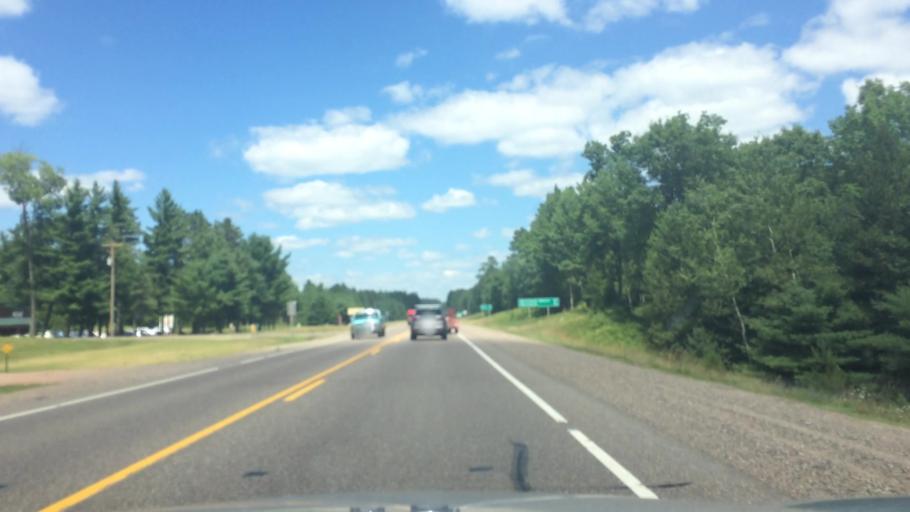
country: US
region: Wisconsin
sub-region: Vilas County
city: Lac du Flambeau
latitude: 45.9243
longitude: -89.6957
